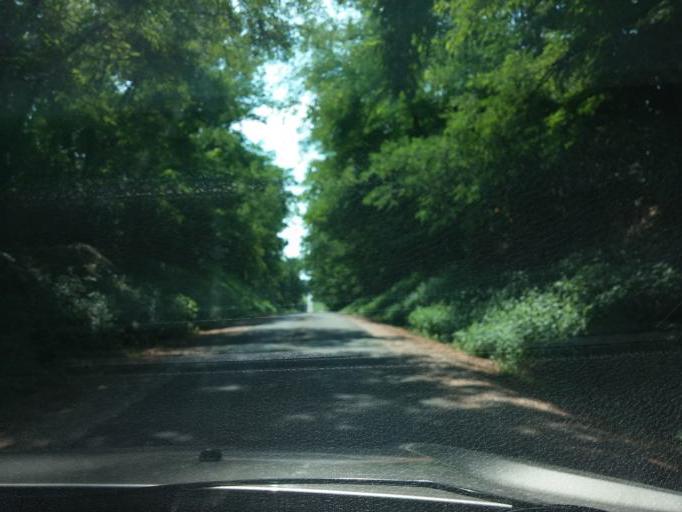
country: HU
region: Somogy
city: Kaposvar
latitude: 46.2587
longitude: 17.8278
